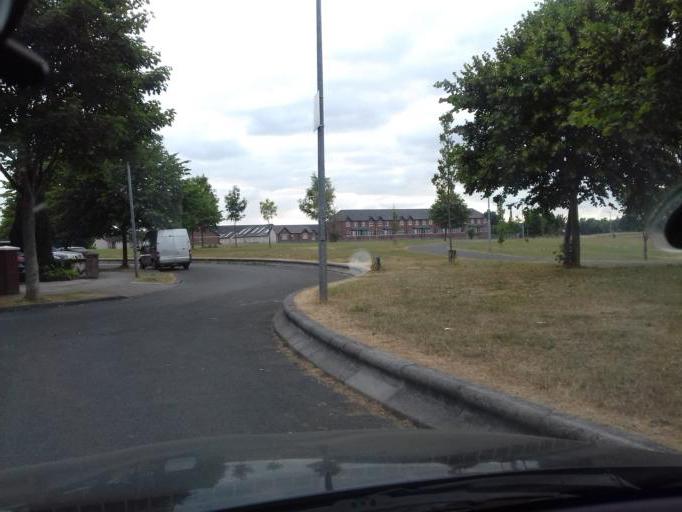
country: IE
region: Leinster
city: Hartstown
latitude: 53.4002
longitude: -6.4242
